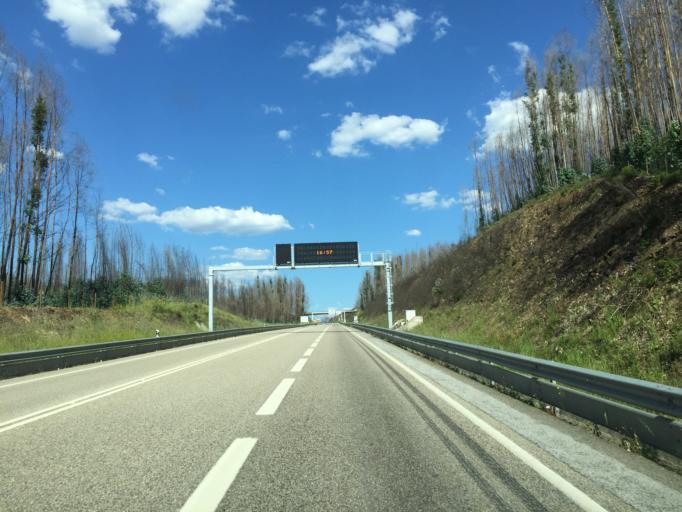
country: PT
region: Leiria
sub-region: Figueiro Dos Vinhos
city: Figueiro dos Vinhos
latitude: 39.9306
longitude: -8.2960
